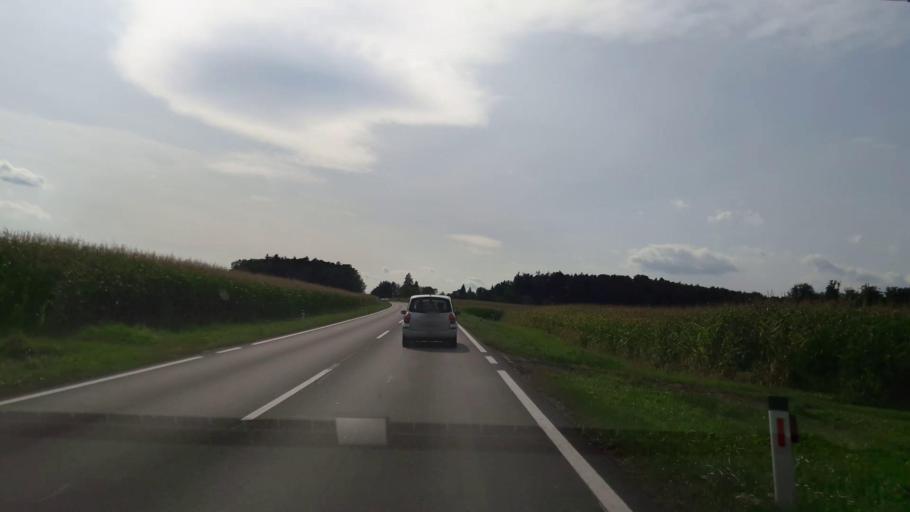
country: AT
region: Styria
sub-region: Politischer Bezirk Hartberg-Fuerstenfeld
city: Kaindorf
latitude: 47.2167
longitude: 15.8880
